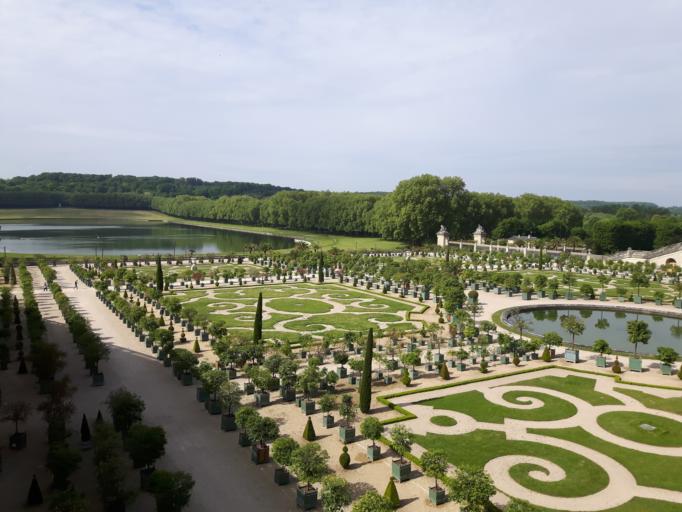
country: FR
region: Ile-de-France
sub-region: Departement des Yvelines
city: Versailles
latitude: 48.8027
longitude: 2.1199
